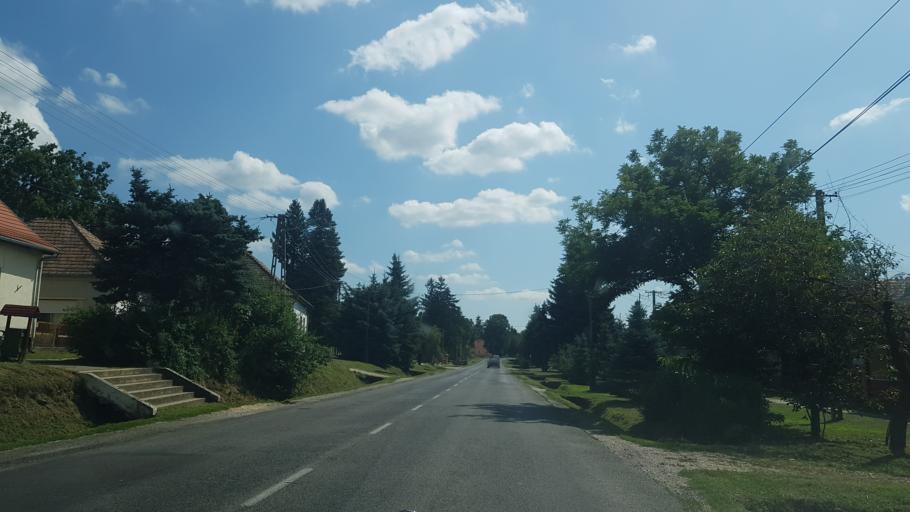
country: HU
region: Somogy
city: Marcali
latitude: 46.5021
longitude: 17.4239
